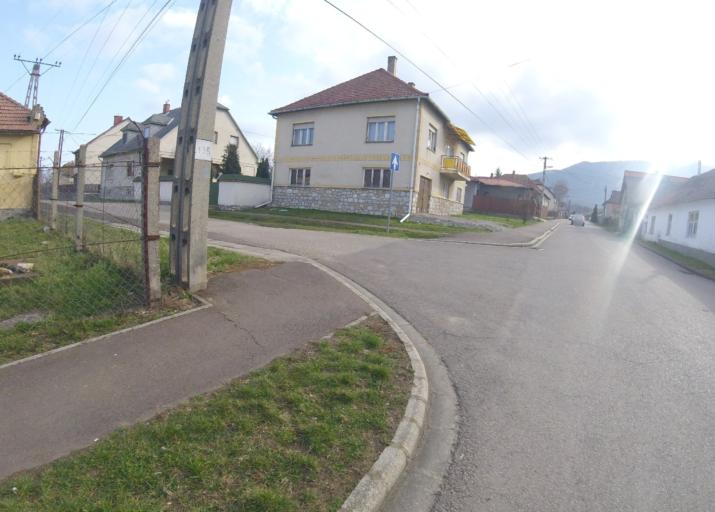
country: HU
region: Heves
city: Belapatfalva
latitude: 48.0534
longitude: 20.3505
